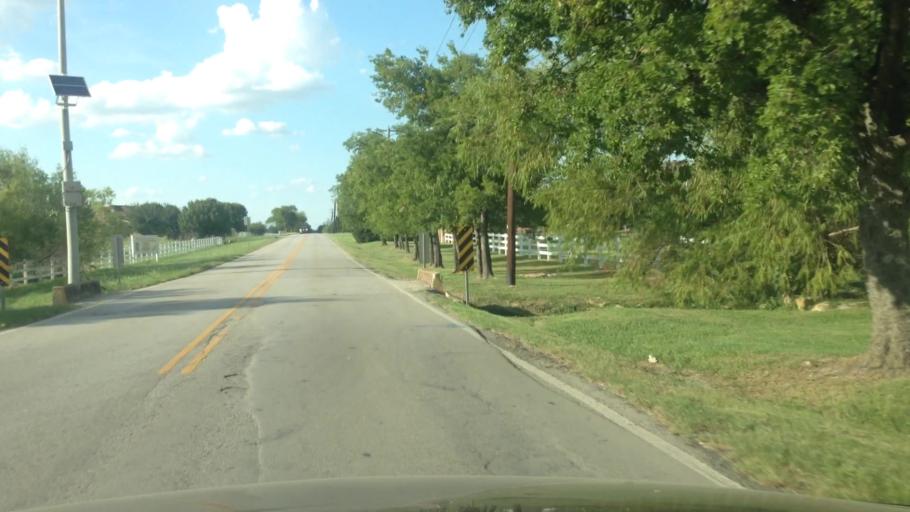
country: US
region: Texas
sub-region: Tarrant County
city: Haslet
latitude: 32.9605
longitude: -97.3919
